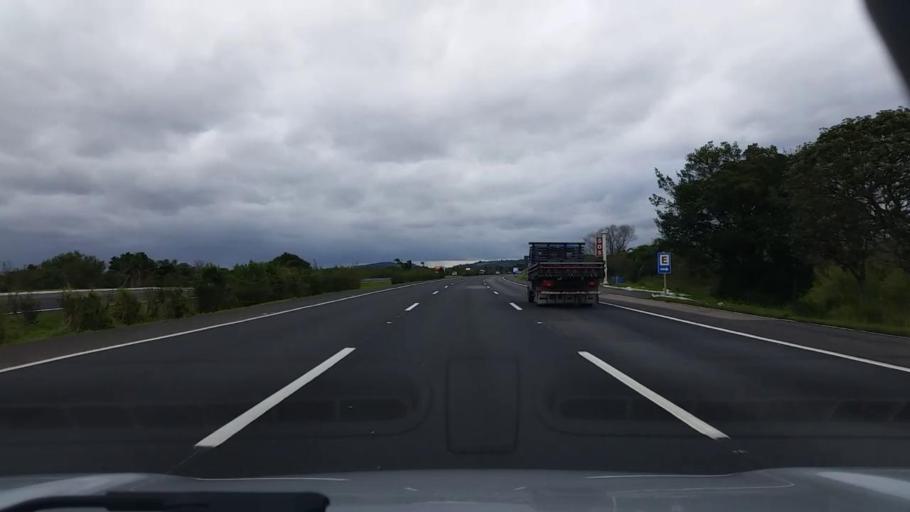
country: BR
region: Rio Grande do Sul
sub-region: Osorio
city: Osorio
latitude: -29.8808
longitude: -50.4345
